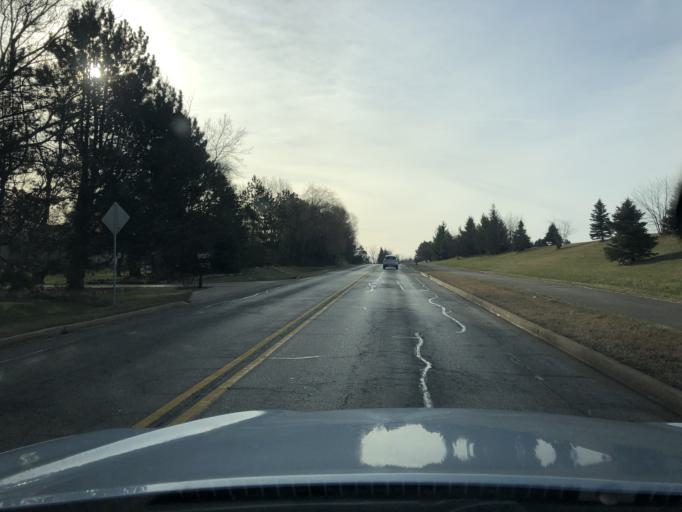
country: US
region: Illinois
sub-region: McHenry County
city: Algonquin
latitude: 42.1562
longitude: -88.3164
